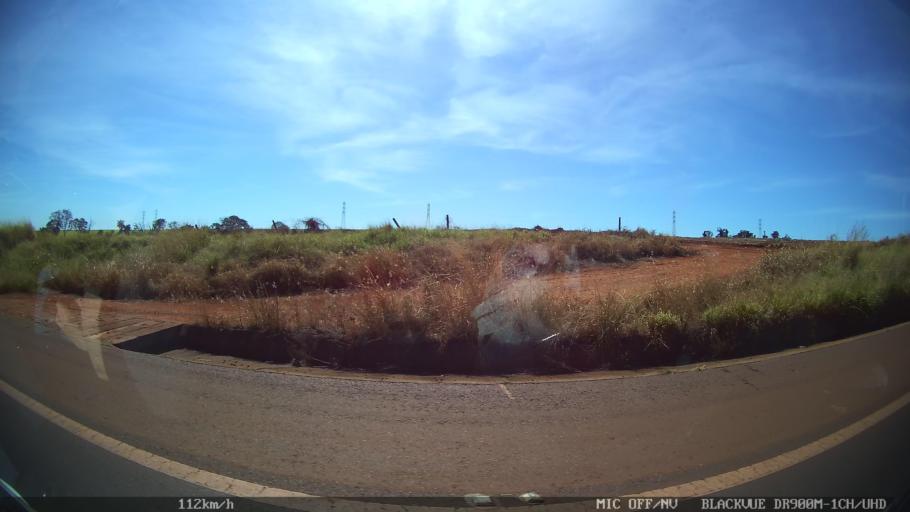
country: BR
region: Sao Paulo
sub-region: Sao Joaquim Da Barra
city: Sao Joaquim da Barra
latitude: -20.5517
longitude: -47.7376
